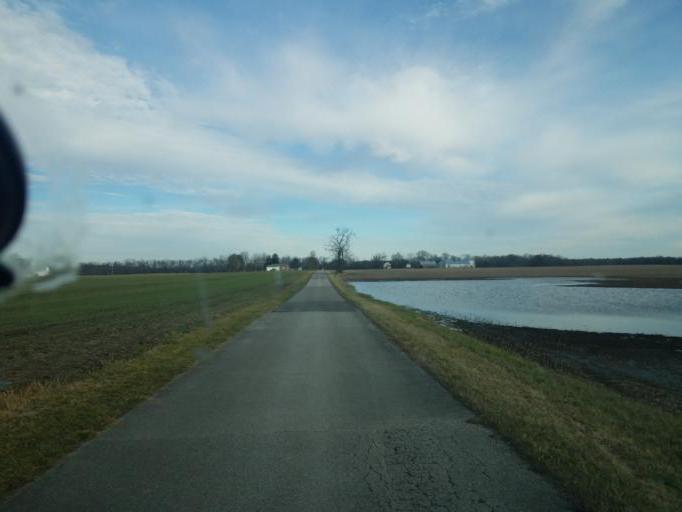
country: US
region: Ohio
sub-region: Morrow County
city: Cardington
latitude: 40.6254
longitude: -82.9426
